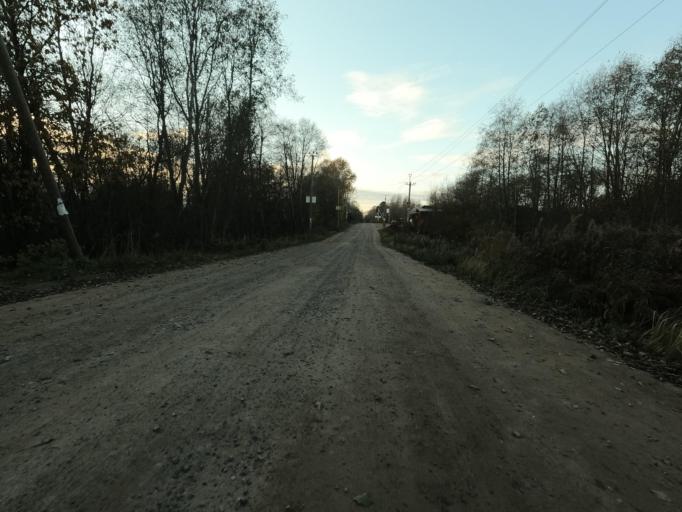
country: RU
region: Leningrad
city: Mga
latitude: 59.7644
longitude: 31.2486
